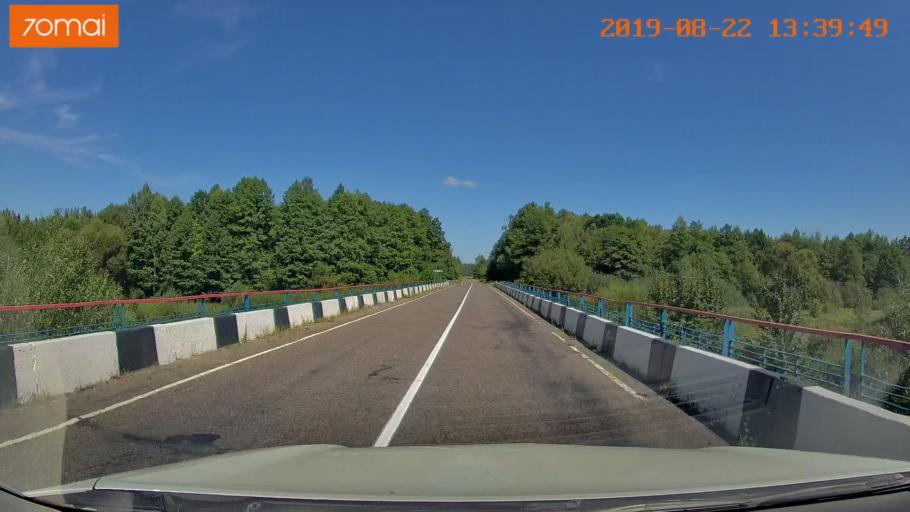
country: BY
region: Minsk
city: Staryya Darohi
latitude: 53.2290
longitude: 28.3558
